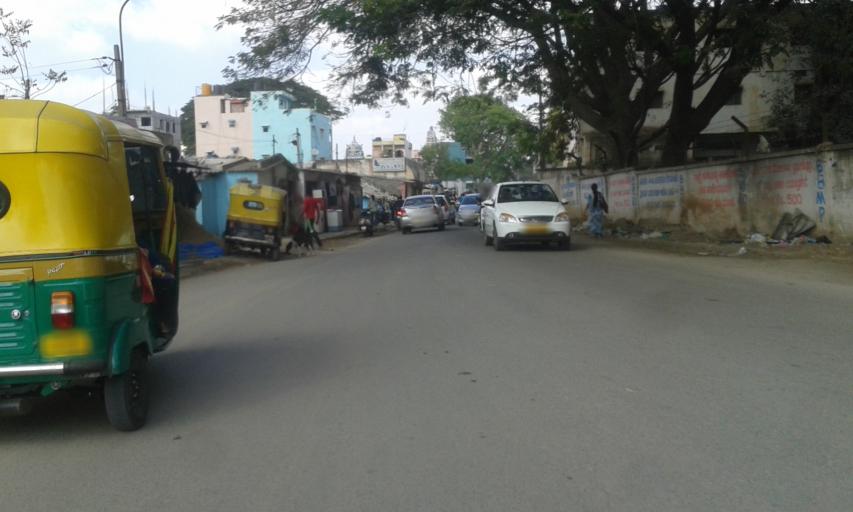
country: IN
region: Karnataka
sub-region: Bangalore Urban
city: Bangalore
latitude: 12.9525
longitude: 77.6202
